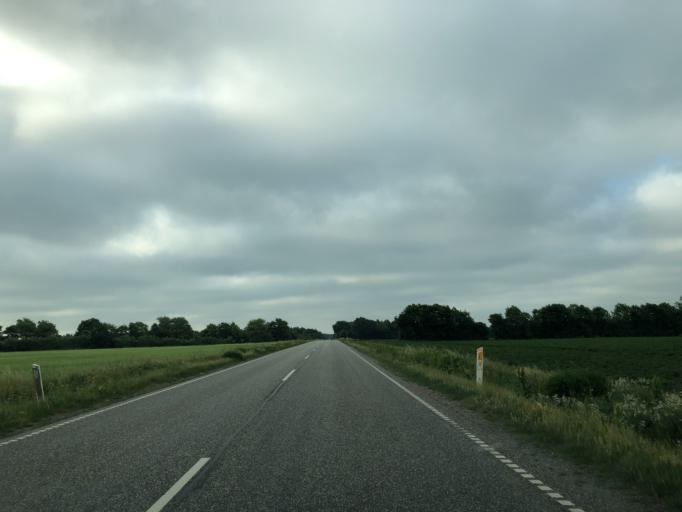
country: DK
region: South Denmark
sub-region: Vejle Kommune
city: Give
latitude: 55.8975
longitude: 9.2057
